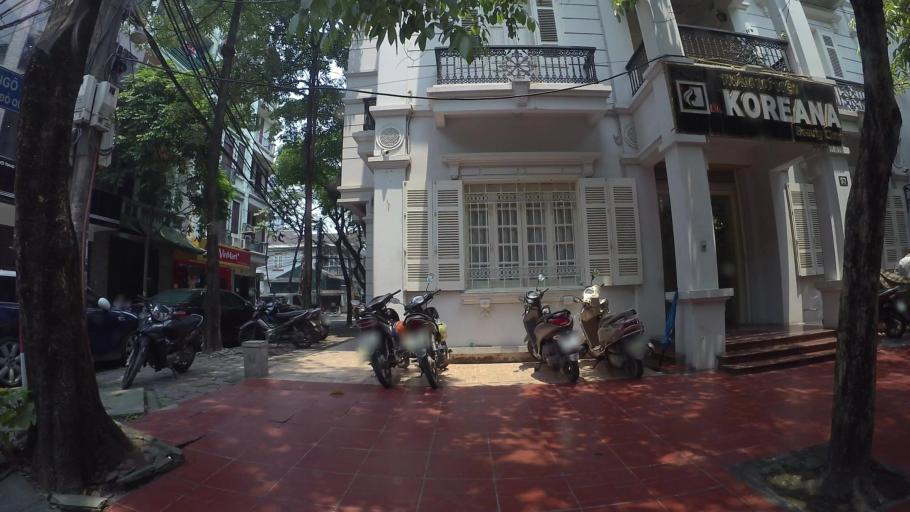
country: VN
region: Ha Noi
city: Thanh Xuan
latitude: 21.0103
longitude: 105.8027
